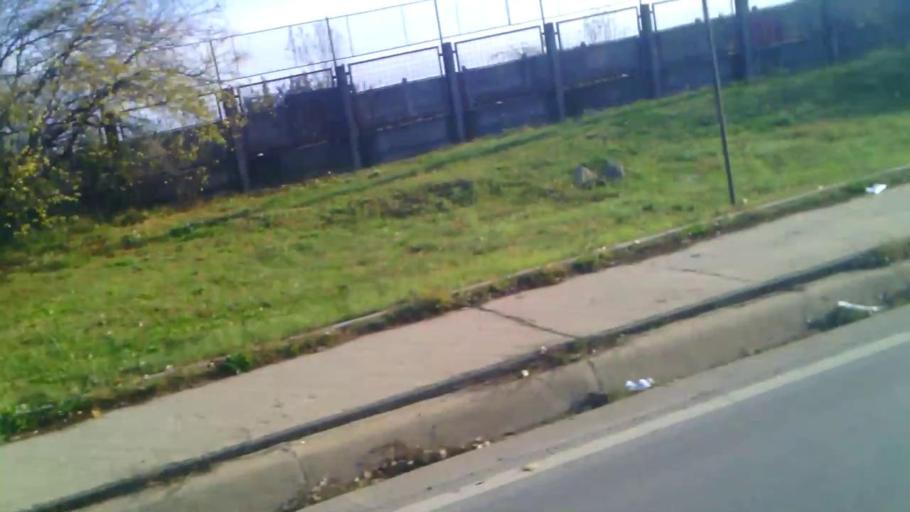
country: RO
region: Ilfov
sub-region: Comuna Popesti-Leordeni
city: Popesti-Leordeni
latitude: 44.3569
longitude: 26.1523
